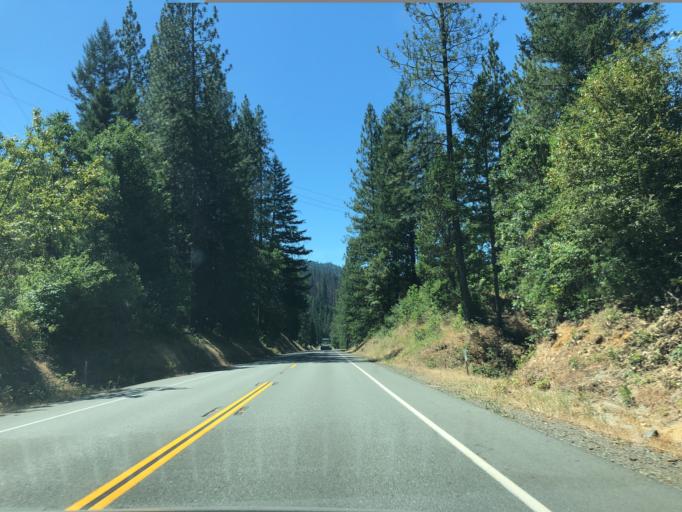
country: US
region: California
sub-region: Trinity County
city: Weaverville
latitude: 40.7076
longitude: -122.9245
